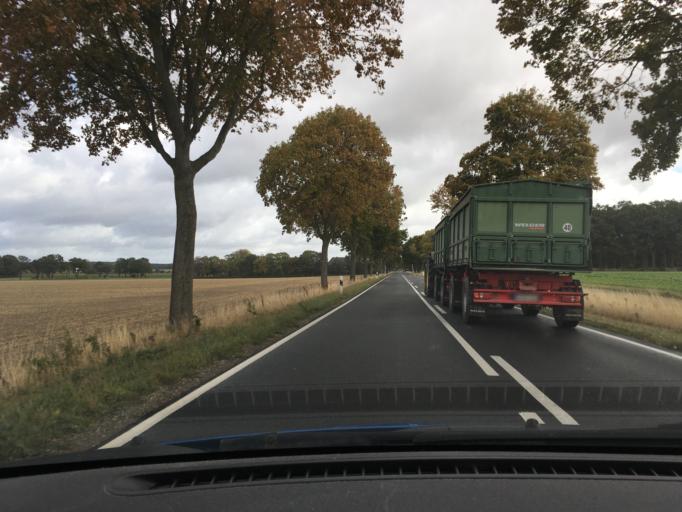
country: DE
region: Lower Saxony
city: Ratzlingen
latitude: 52.9579
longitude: 10.6539
